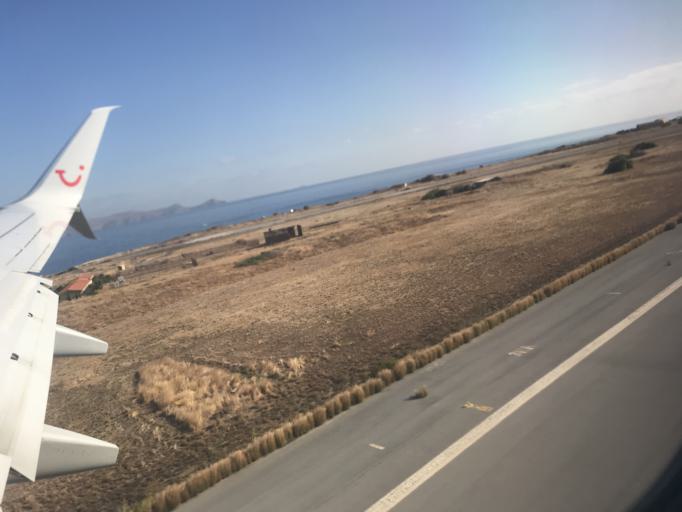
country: GR
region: Crete
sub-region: Nomos Irakleiou
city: Nea Alikarnassos
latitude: 35.3407
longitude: 25.1713
